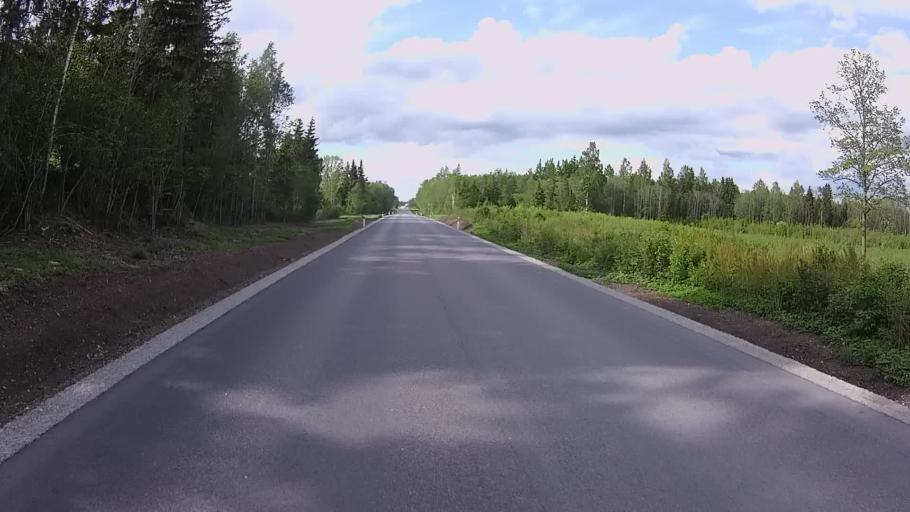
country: EE
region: Laeaene-Virumaa
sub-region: Vinni vald
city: Vinni
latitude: 59.0886
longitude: 26.6248
